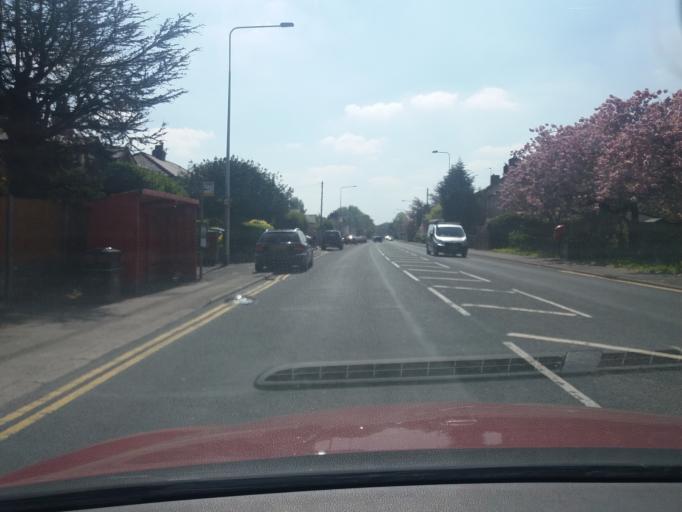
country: GB
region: England
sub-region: Lancashire
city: Clayton-le-Woods
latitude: 53.7039
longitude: -2.6396
